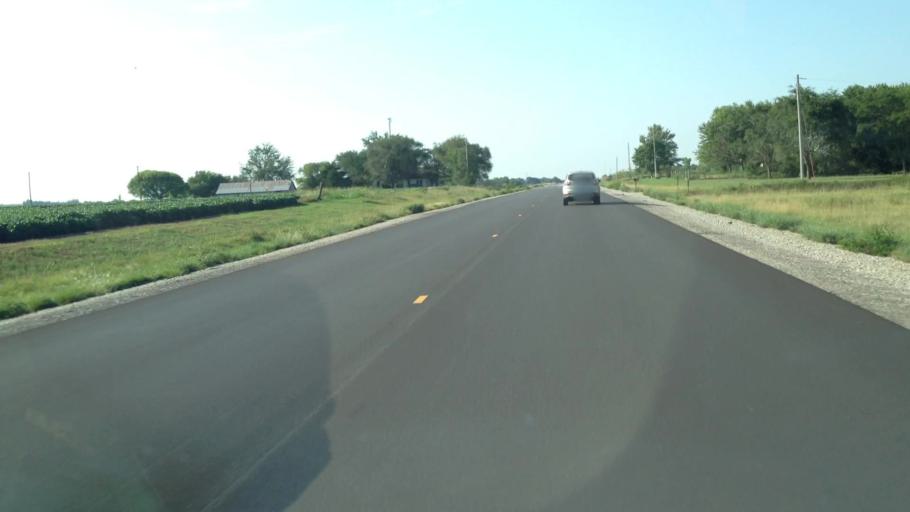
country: US
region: Kansas
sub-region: Anderson County
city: Garnett
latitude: 38.3823
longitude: -95.2488
